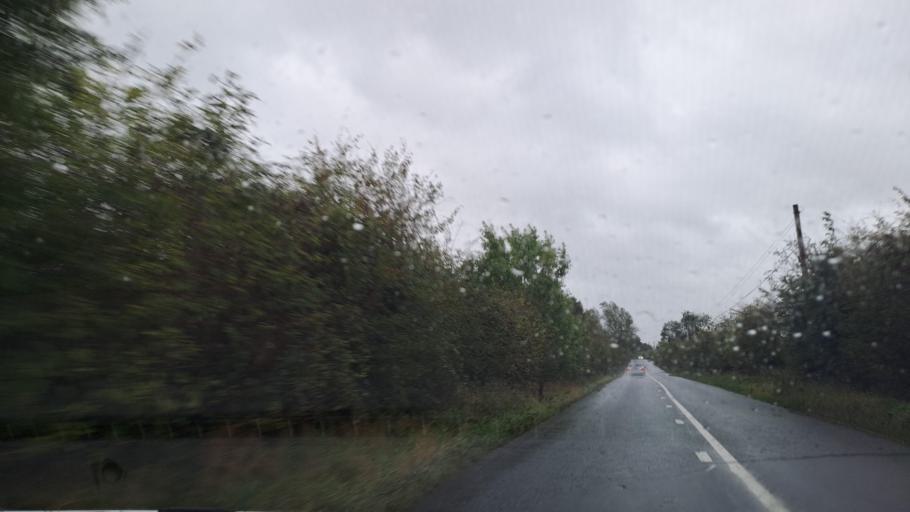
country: GB
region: Northern Ireland
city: Crossmaglen
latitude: 53.9718
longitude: -6.5985
